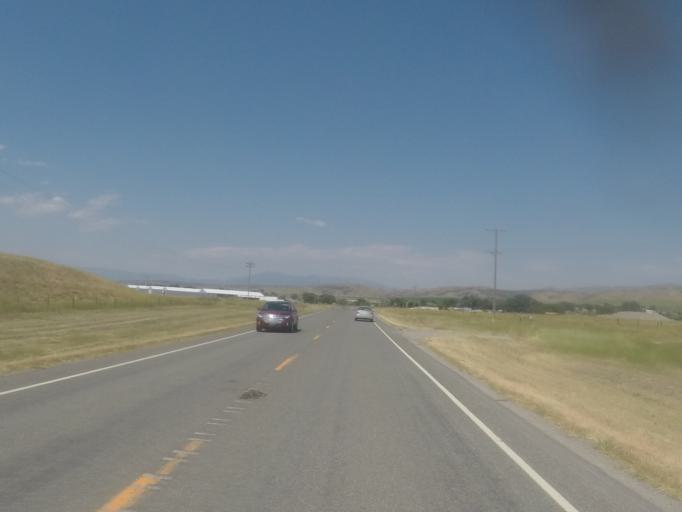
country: US
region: Montana
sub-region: Broadwater County
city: Townsend
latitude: 46.1662
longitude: -111.4520
